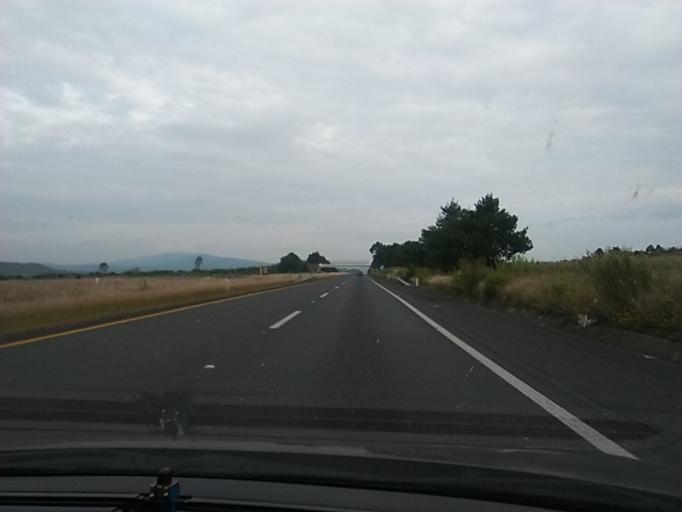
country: MX
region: Michoacan
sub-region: Puruandiro
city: San Lorenzo
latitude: 19.9596
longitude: -101.6685
